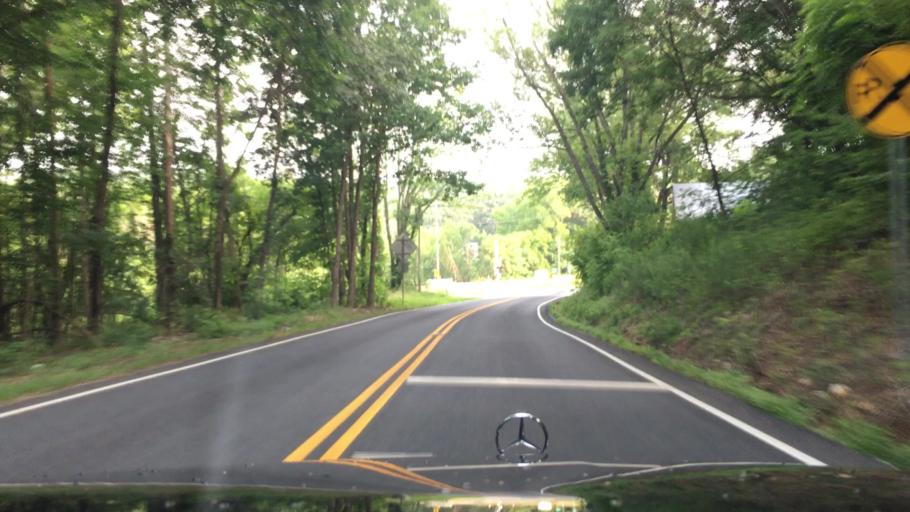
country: US
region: Virginia
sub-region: Campbell County
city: Timberlake
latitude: 37.2340
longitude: -79.2848
